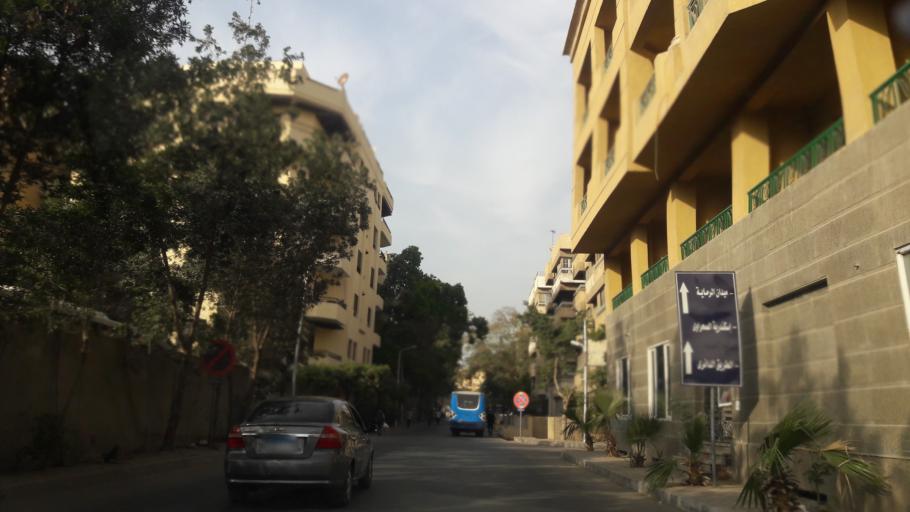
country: EG
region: Al Jizah
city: Al Jizah
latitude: 29.9881
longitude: 31.1326
